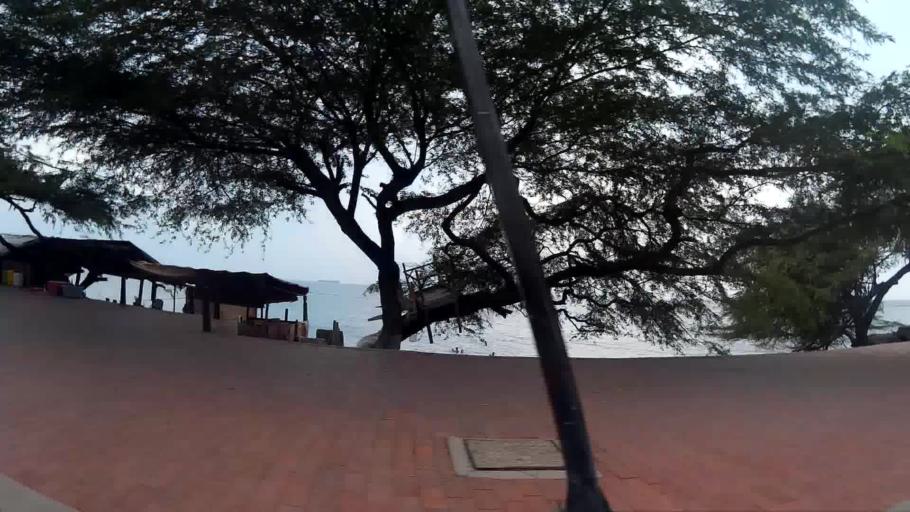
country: CO
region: Magdalena
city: Cienaga
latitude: 11.1230
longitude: -74.2313
